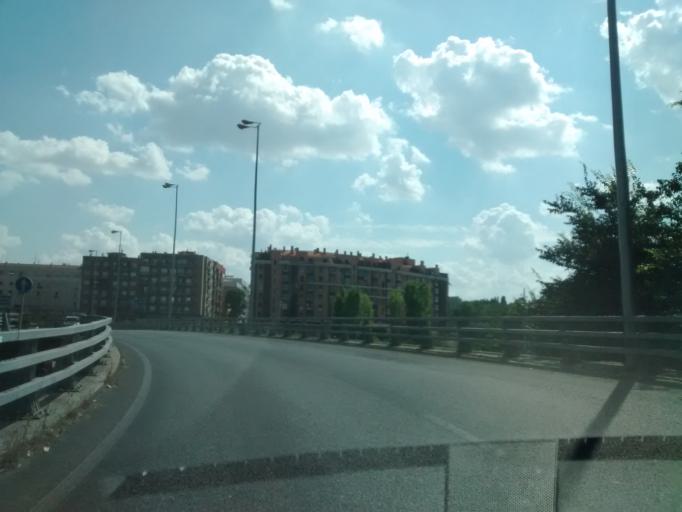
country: ES
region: Madrid
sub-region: Provincia de Madrid
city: Carabanchel
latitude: 40.4008
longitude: -3.7172
